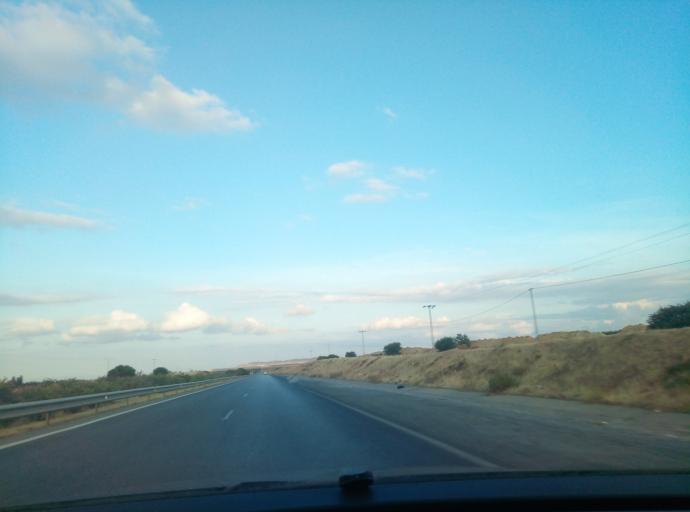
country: TN
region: Manouba
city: El Battan
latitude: 36.6593
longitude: 9.8260
